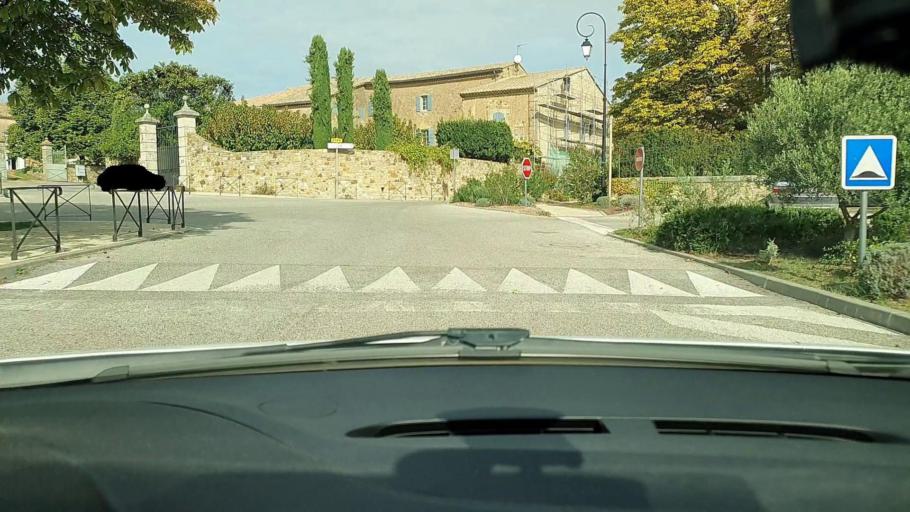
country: FR
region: Languedoc-Roussillon
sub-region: Departement du Gard
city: Saint-Quentin-la-Poterie
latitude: 44.1109
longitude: 4.4146
